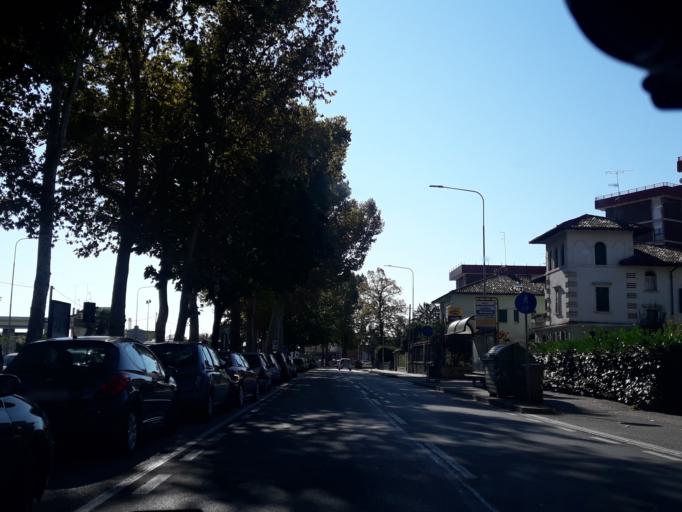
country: IT
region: Friuli Venezia Giulia
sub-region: Provincia di Udine
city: Udine
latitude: 46.0602
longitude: 13.2478
